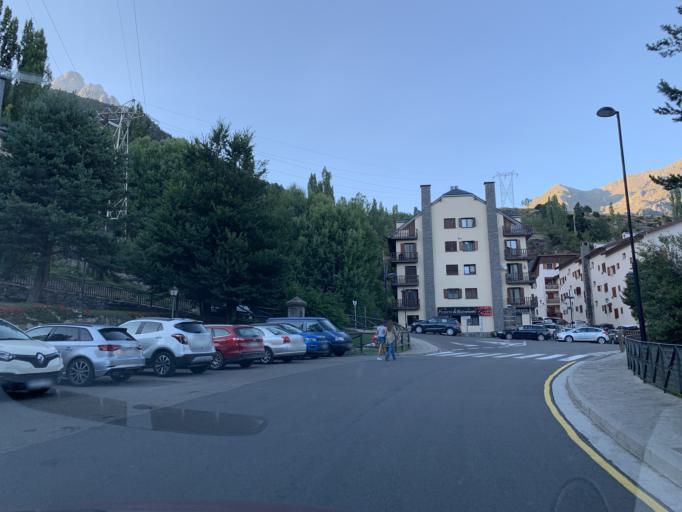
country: ES
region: Aragon
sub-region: Provincia de Huesca
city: Sallent de Gallego
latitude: 42.7717
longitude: -0.3351
